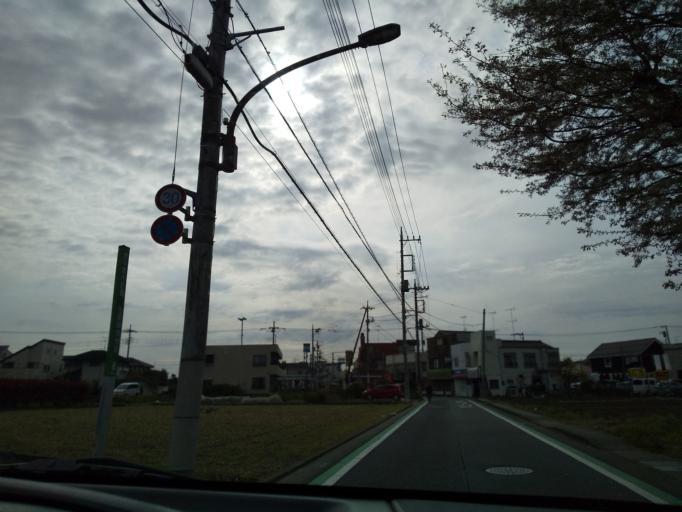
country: JP
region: Tokyo
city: Kokubunji
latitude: 35.6624
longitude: 139.4488
